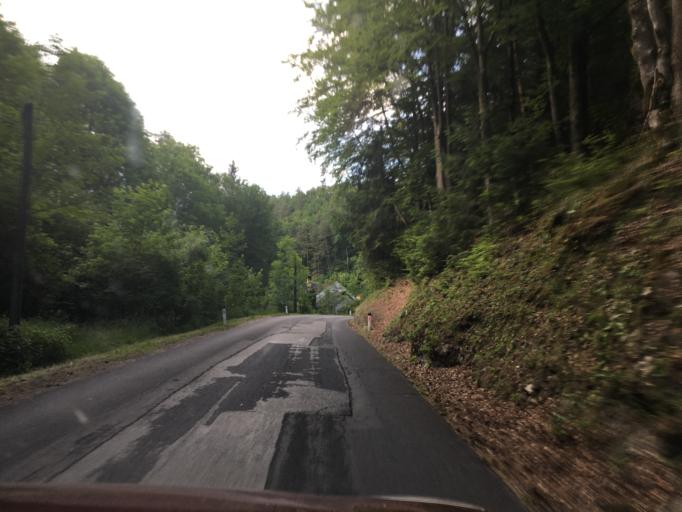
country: AT
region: Upper Austria
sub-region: Politischer Bezirk Urfahr-Umgebung
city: Alberndorf in der Riedmark
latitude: 48.4053
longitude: 14.3994
